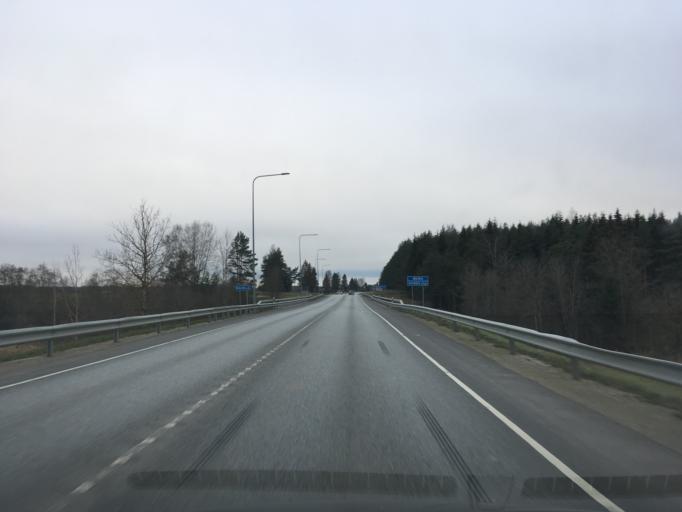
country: EE
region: Laeaene-Virumaa
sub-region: Viru-Nigula vald
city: Kunda
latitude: 59.3743
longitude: 26.5827
